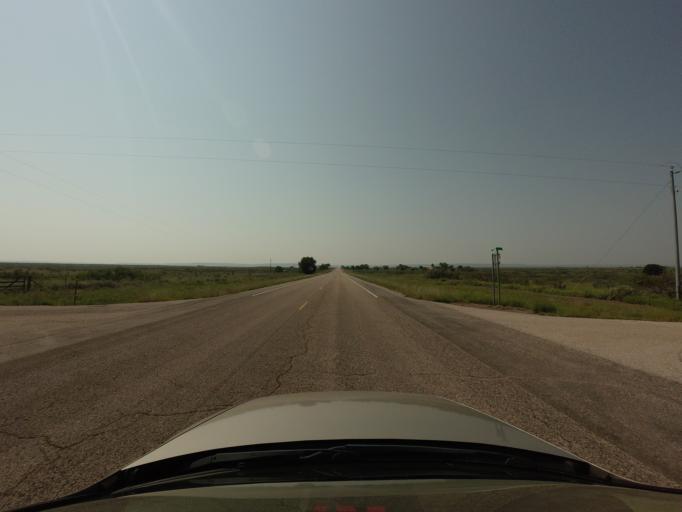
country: US
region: New Mexico
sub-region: Quay County
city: Tucumcari
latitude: 34.9384
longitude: -103.7602
